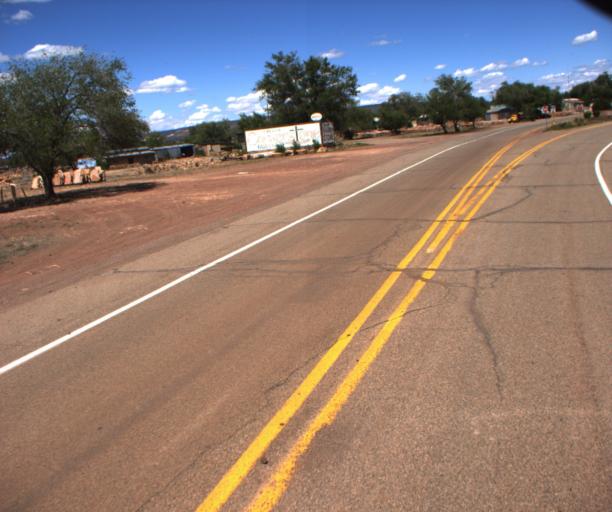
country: US
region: Arizona
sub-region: Coconino County
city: Williams
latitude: 35.2242
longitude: -112.4917
